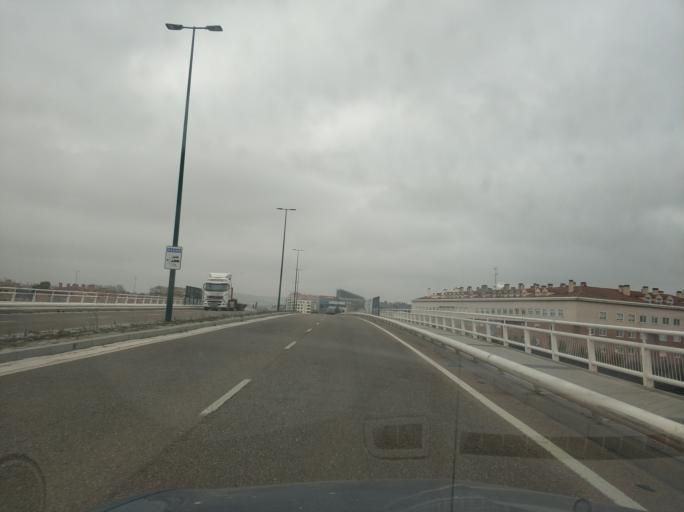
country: ES
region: Castille and Leon
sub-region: Provincia de Valladolid
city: Valladolid
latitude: 41.6210
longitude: -4.7399
